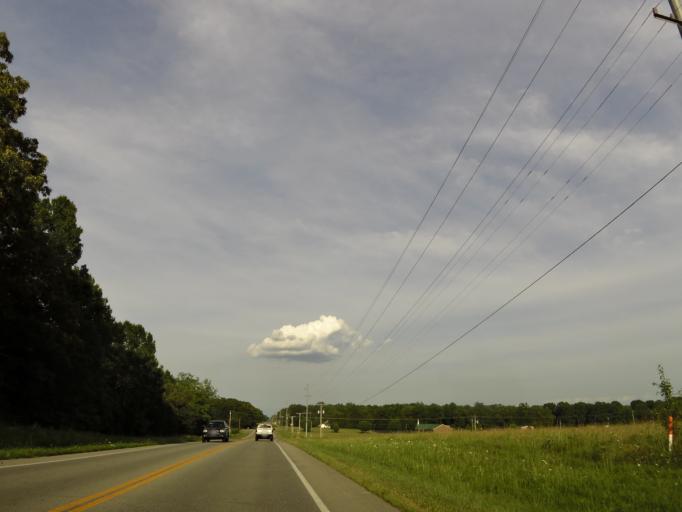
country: US
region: Tennessee
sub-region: Dickson County
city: Dickson
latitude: 36.0905
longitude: -87.4995
